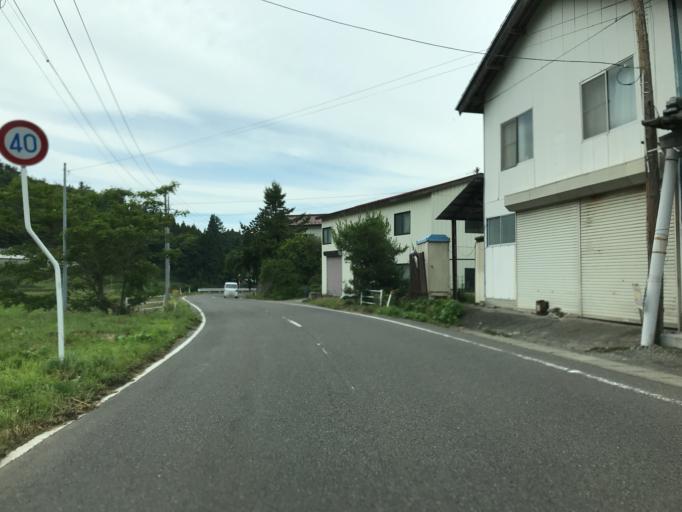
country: JP
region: Fukushima
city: Funehikimachi-funehiki
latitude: 37.3995
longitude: 140.6941
